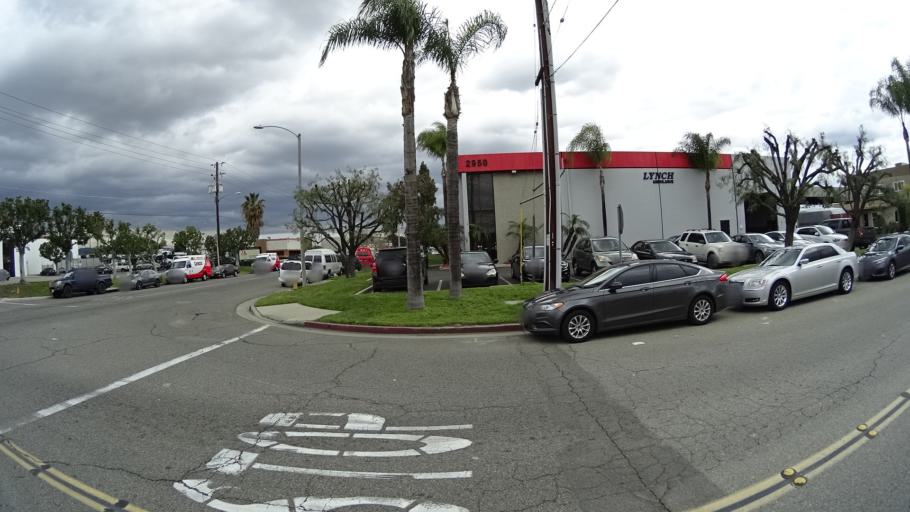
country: US
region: California
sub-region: Orange County
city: Placentia
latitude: 33.8597
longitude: -117.8673
